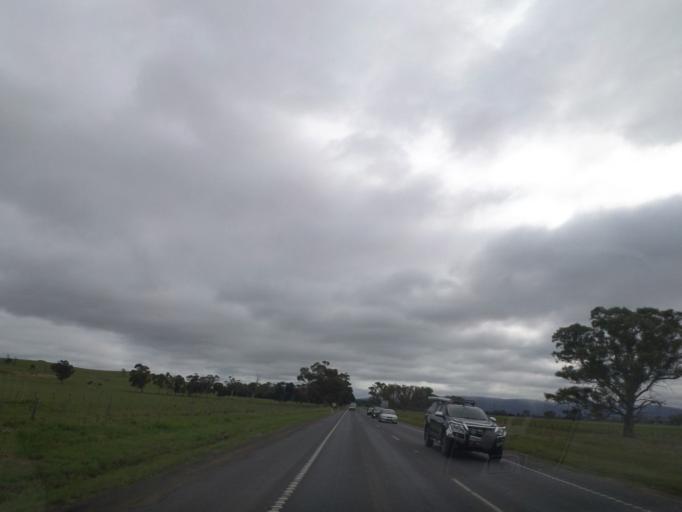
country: AU
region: Victoria
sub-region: Whittlesea
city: Whittlesea
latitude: -37.5564
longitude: 145.1096
